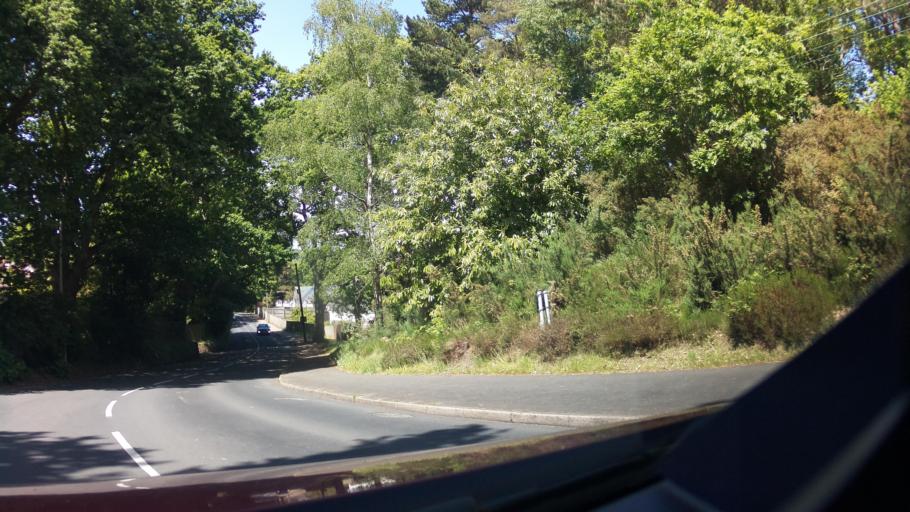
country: GB
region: England
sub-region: Devon
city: Budleigh Salterton
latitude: 50.6300
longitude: -3.3388
